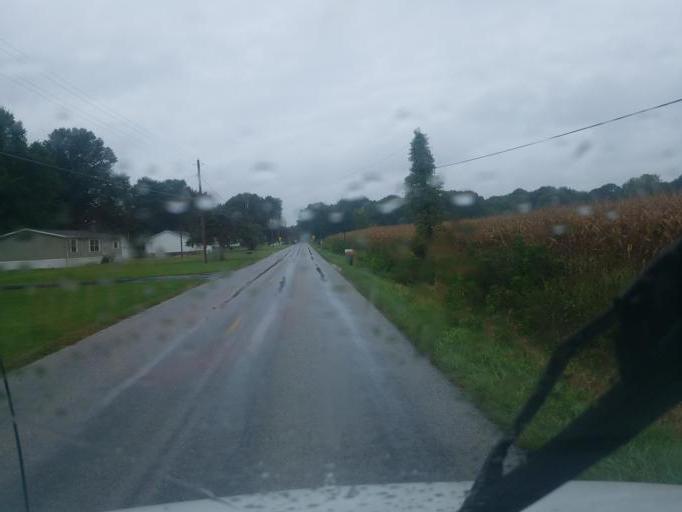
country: US
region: Ohio
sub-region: Wayne County
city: Creston
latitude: 40.9822
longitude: -81.8707
